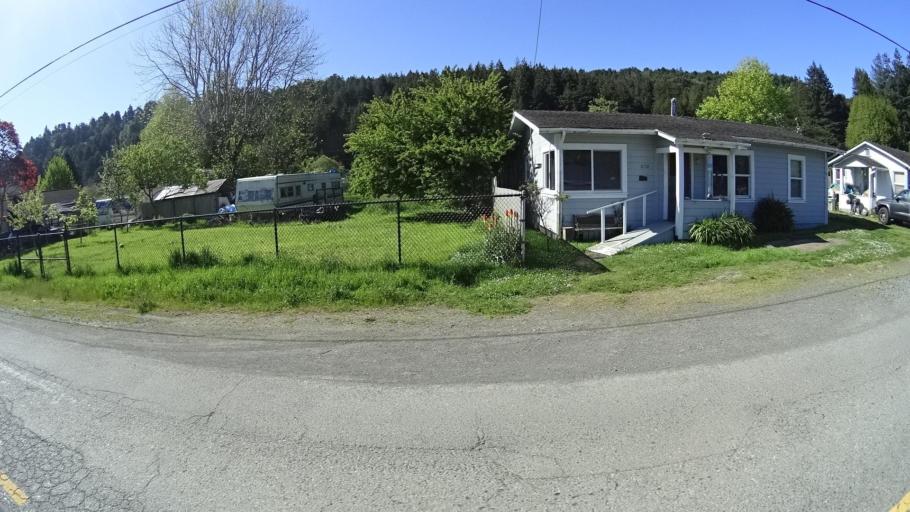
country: US
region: California
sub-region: Humboldt County
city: Rio Dell
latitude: 40.5070
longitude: -124.1228
